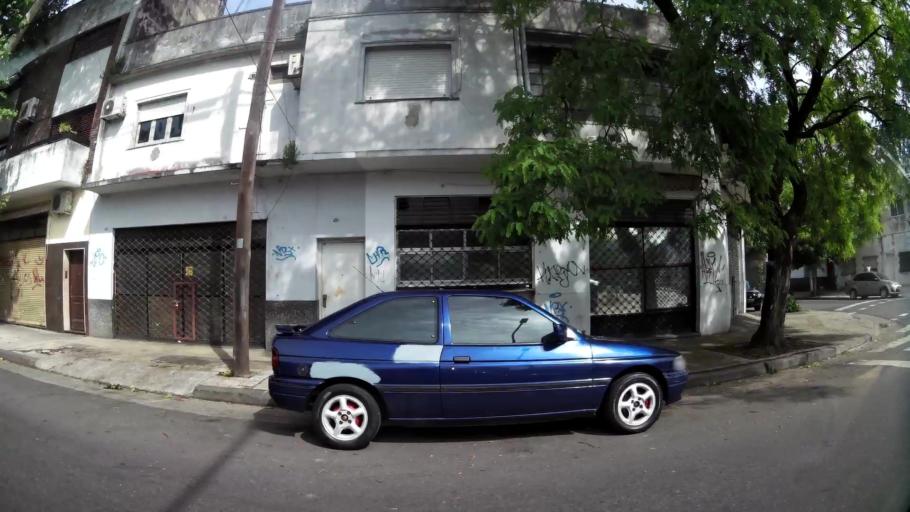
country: AR
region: Buenos Aires F.D.
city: Villa Lugano
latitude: -34.6607
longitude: -58.5038
